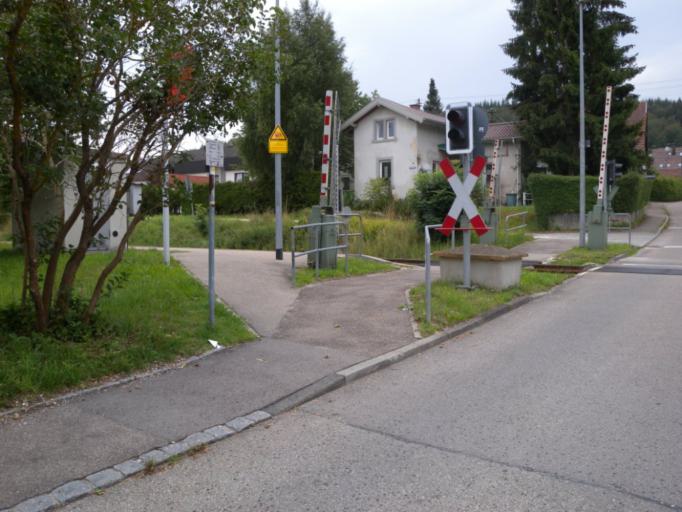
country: DE
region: Baden-Wuerttemberg
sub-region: Regierungsbezirk Stuttgart
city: Konigsbronn
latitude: 48.7308
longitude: 10.1359
